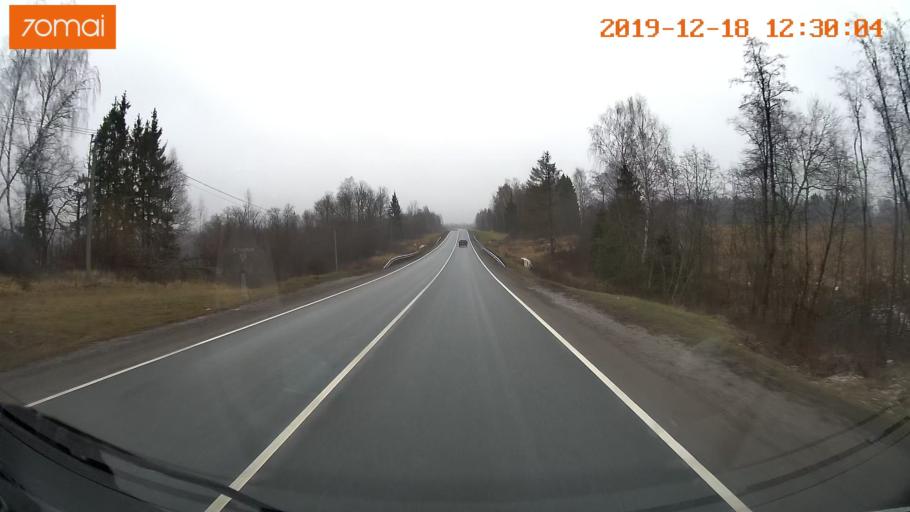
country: RU
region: Moskovskaya
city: Novopetrovskoye
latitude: 56.0850
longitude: 36.5245
